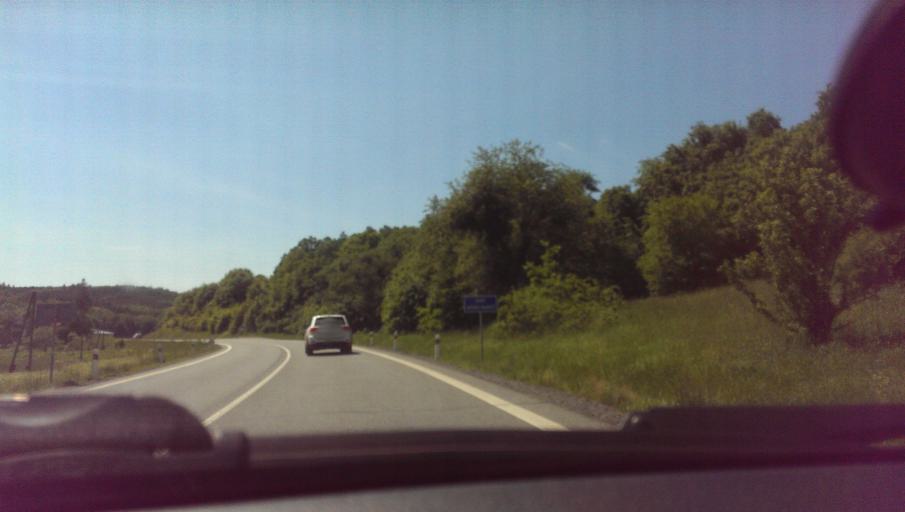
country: CZ
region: Zlin
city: Brezolupy
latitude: 49.1427
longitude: 17.6048
